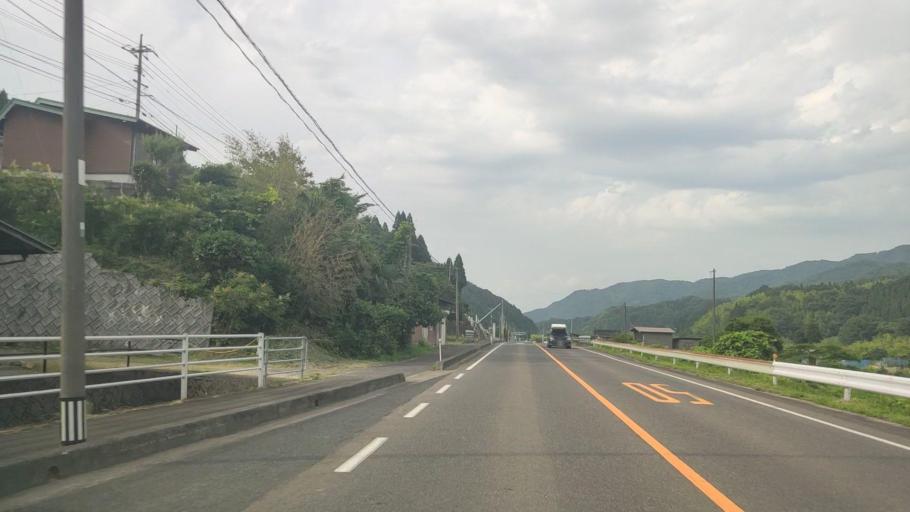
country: JP
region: Tottori
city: Kurayoshi
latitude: 35.3463
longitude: 133.8412
